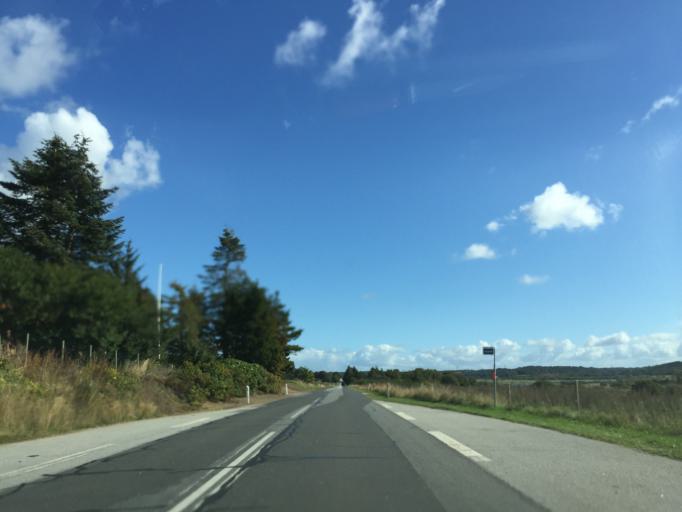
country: DK
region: Central Jutland
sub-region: Viborg Kommune
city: Viborg
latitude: 56.4398
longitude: 9.5181
